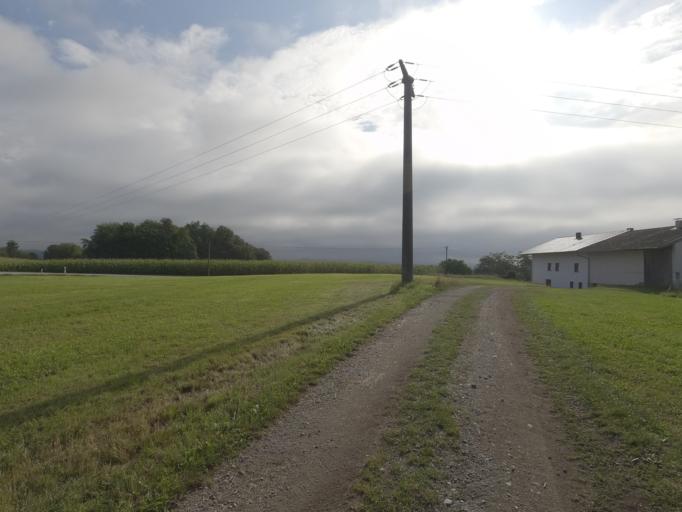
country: DE
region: Bavaria
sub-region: Lower Bavaria
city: Niederalteich
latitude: 48.7995
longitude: 13.0240
